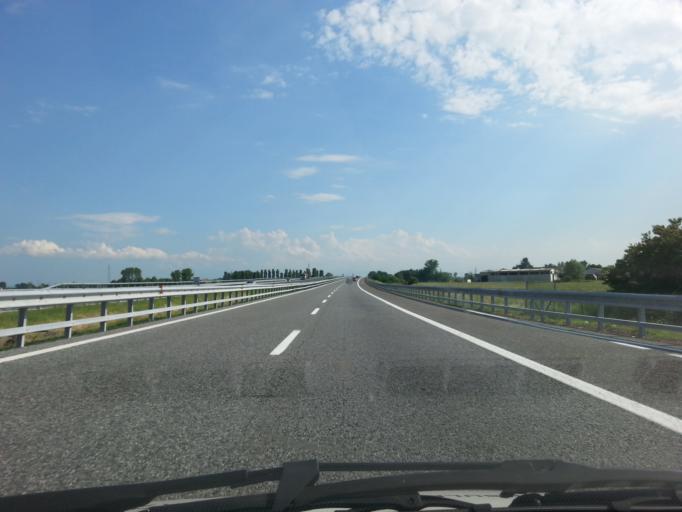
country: IT
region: Piedmont
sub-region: Provincia di Cuneo
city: Caramagna Piemonte
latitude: 44.7870
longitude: 7.7531
